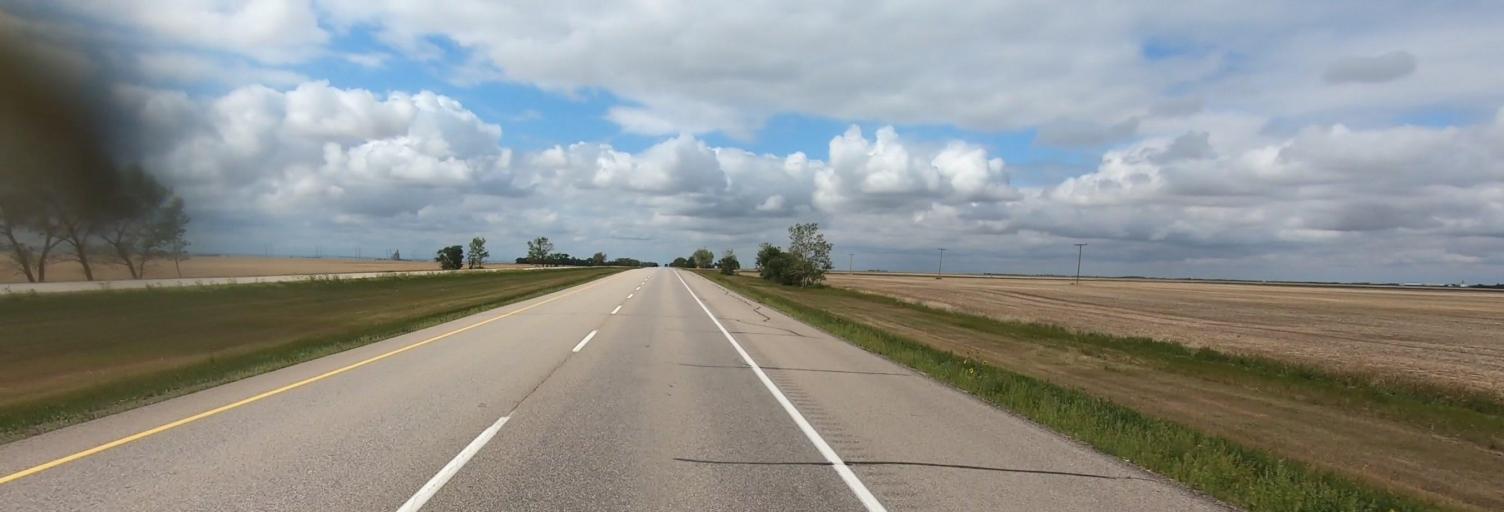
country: CA
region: Saskatchewan
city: Moose Jaw
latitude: 50.3973
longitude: -105.2776
